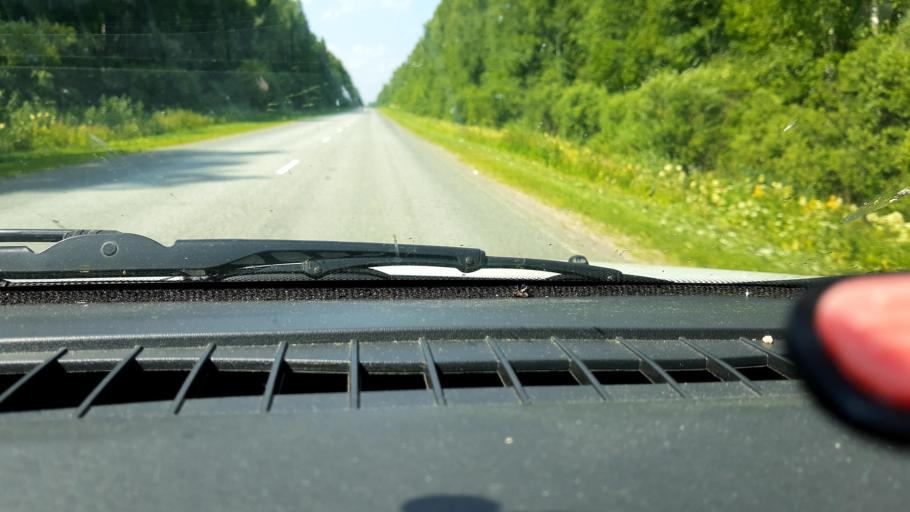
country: RU
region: Nizjnij Novgorod
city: Sharanga
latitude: 57.2334
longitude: 46.4915
